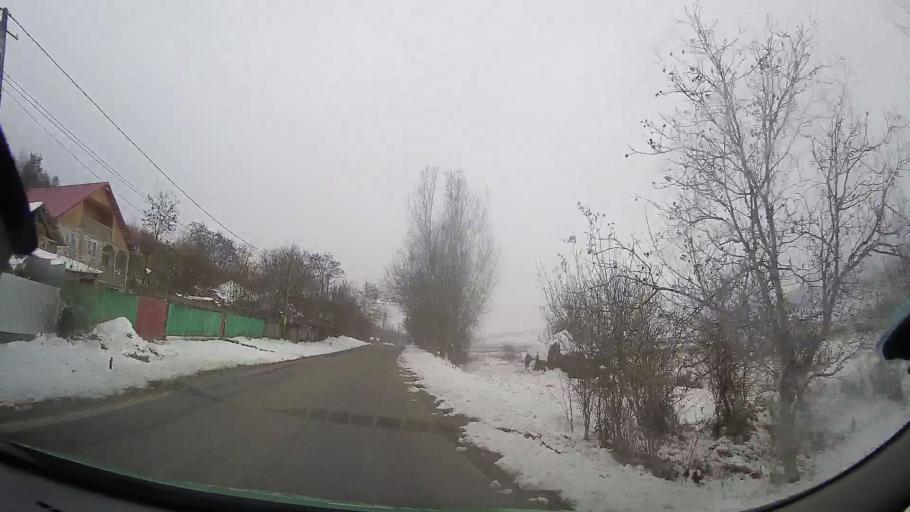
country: RO
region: Bacau
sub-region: Comuna Vultureni
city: Vultureni
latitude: 46.3449
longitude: 27.2905
